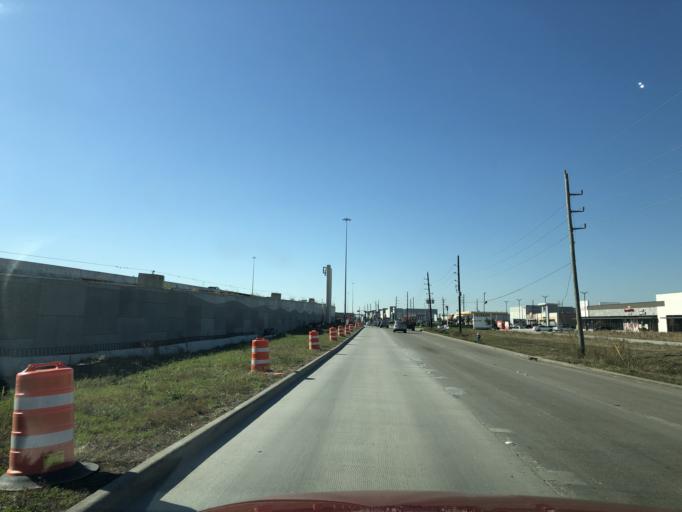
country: US
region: Texas
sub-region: Brazoria County
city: Brookside Village
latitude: 29.5984
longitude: -95.3650
